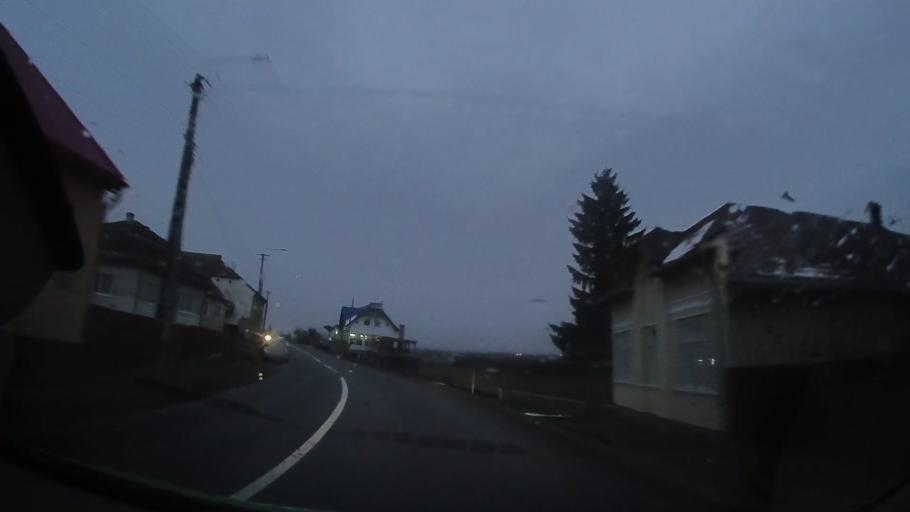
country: RO
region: Harghita
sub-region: Comuna Remetea
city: Remetea
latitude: 46.7941
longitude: 25.4551
